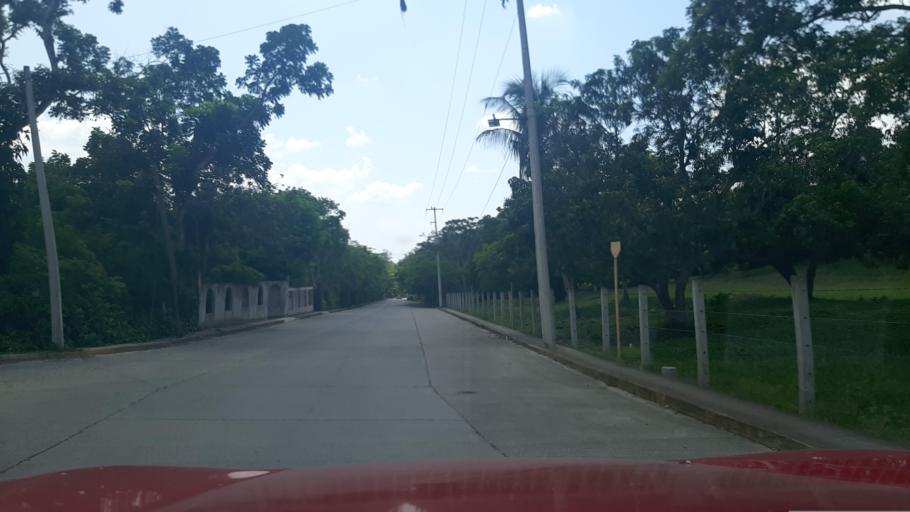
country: MX
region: Veracruz
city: Coatzintla
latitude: 20.4975
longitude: -97.4344
